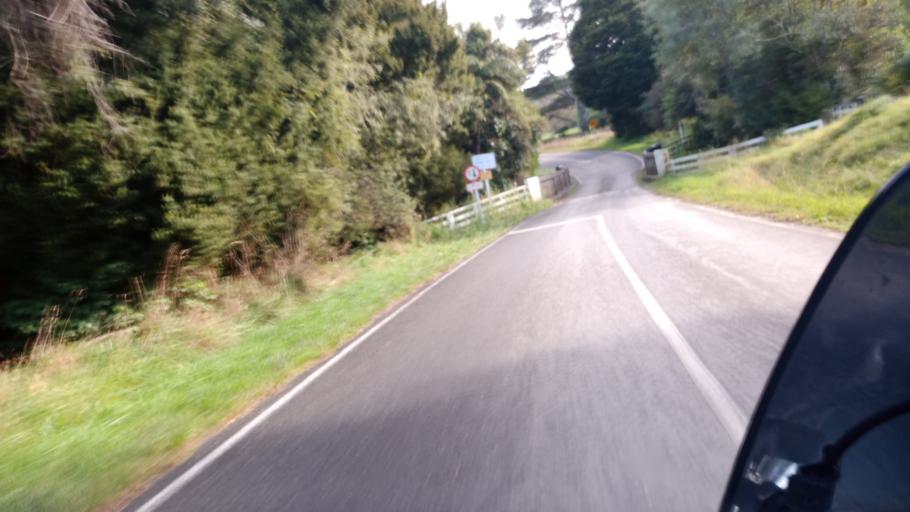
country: NZ
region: Gisborne
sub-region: Gisborne District
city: Gisborne
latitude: -38.5383
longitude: 177.5604
